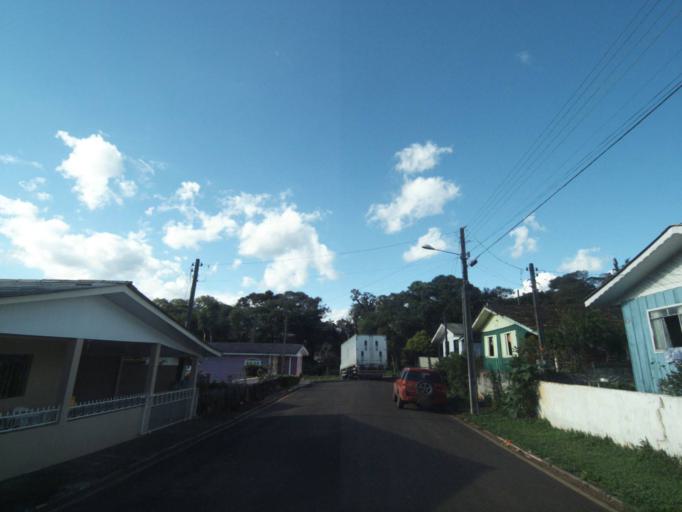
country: BR
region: Parana
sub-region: Uniao Da Vitoria
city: Uniao da Vitoria
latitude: -26.1601
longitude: -51.5371
